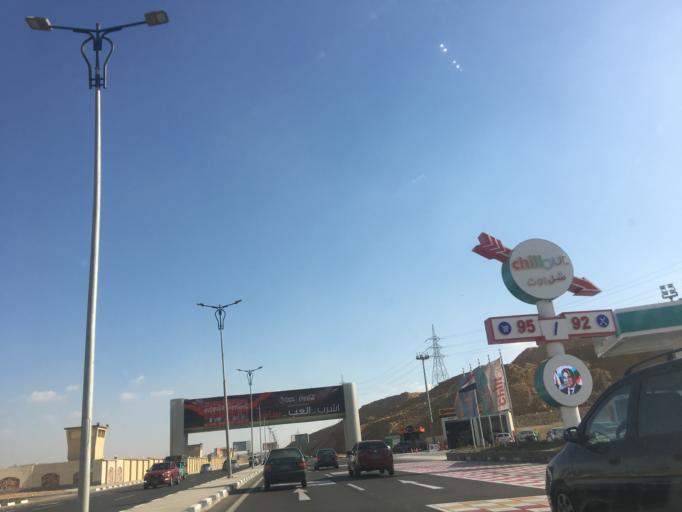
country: EG
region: Muhafazat al Qahirah
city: Cairo
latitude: 30.0216
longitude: 31.3291
